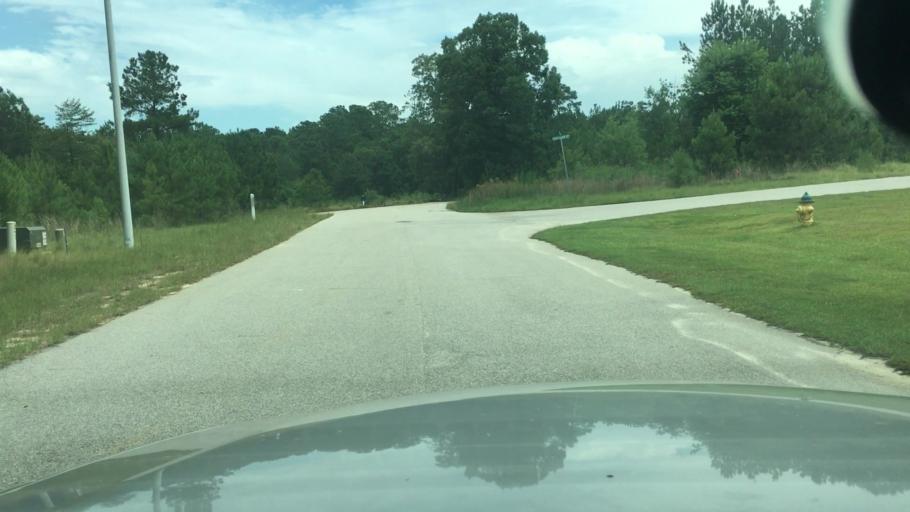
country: US
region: North Carolina
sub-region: Cumberland County
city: Hope Mills
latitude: 34.9604
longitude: -78.8965
